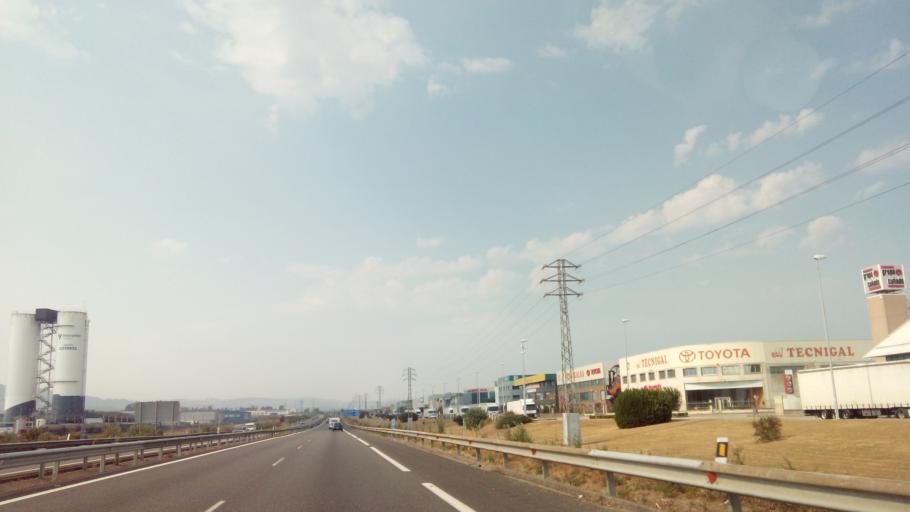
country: ES
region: Galicia
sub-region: Provincia de Pontevedra
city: Porrino
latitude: 42.1208
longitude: -8.6219
